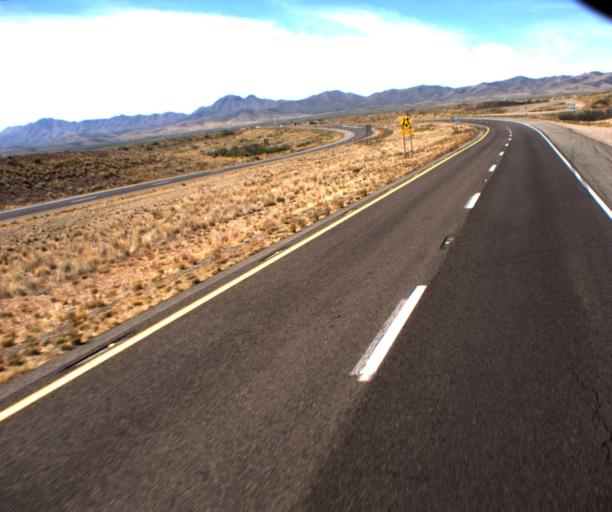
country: US
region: Arizona
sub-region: Cochise County
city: Willcox
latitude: 32.3651
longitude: -109.6800
